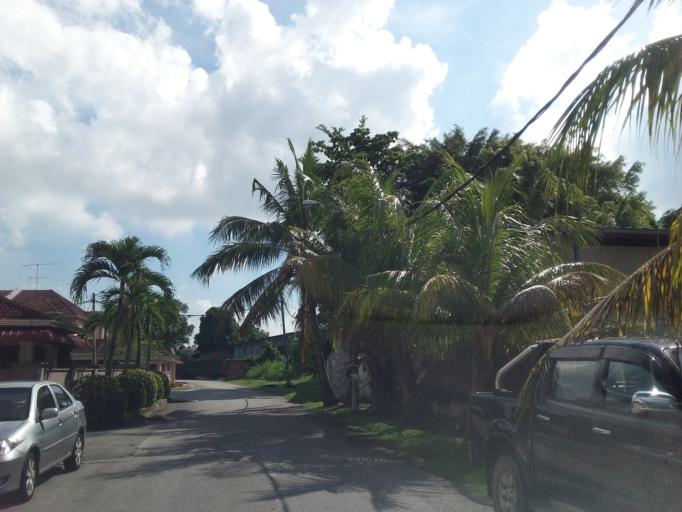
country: MY
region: Johor
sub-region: Daerah Batu Pahat
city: Batu Pahat
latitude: 1.8415
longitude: 102.9307
